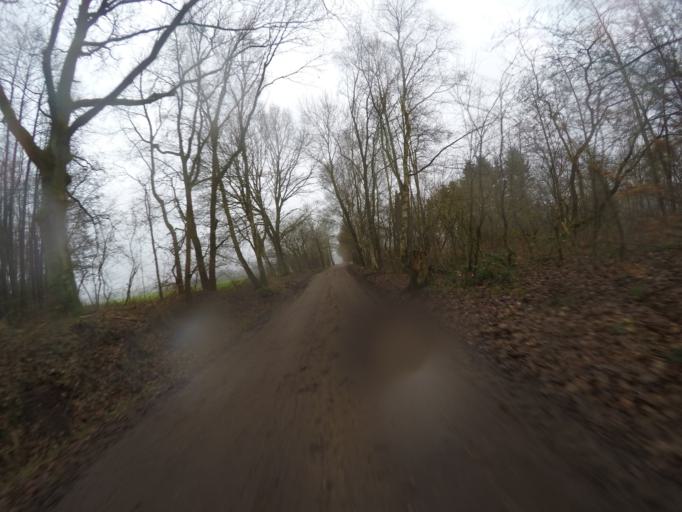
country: DE
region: Schleswig-Holstein
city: Ellerau
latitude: 53.7439
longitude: 9.9244
